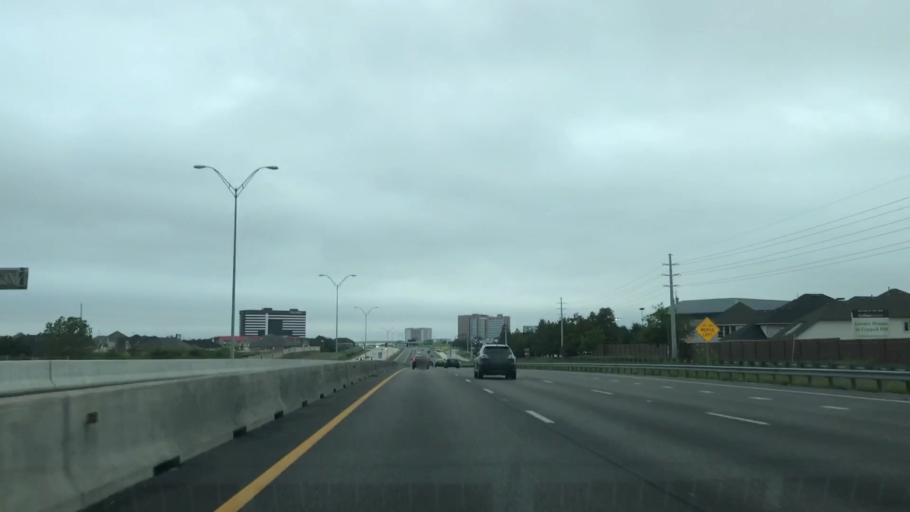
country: US
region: Texas
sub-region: Dallas County
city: Coppell
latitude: 32.9095
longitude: -96.9983
